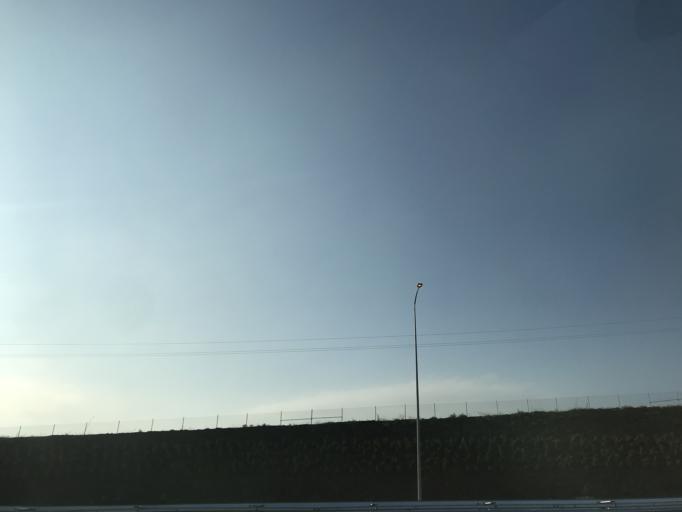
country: TR
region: Balikesir
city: Gobel
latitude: 40.0453
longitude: 28.2246
